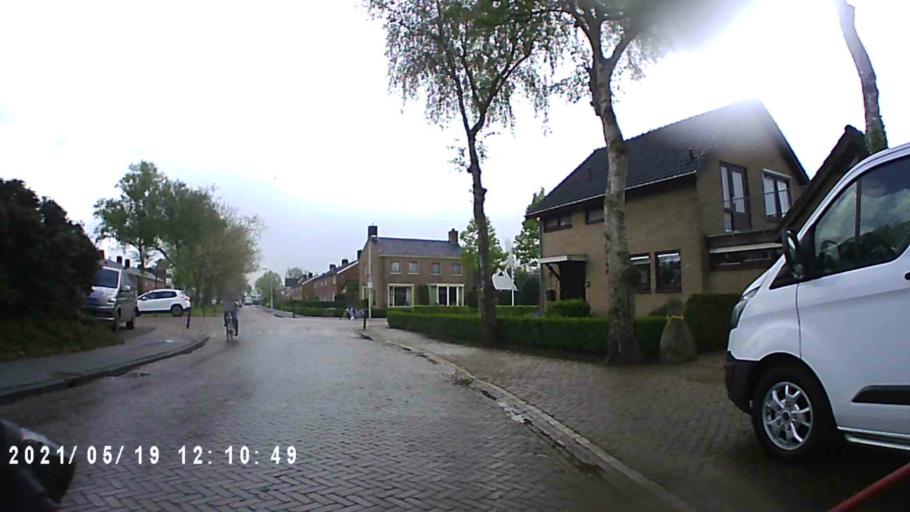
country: NL
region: Friesland
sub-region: Gemeente Achtkarspelen
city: Buitenpost
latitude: 53.2520
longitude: 6.1456
